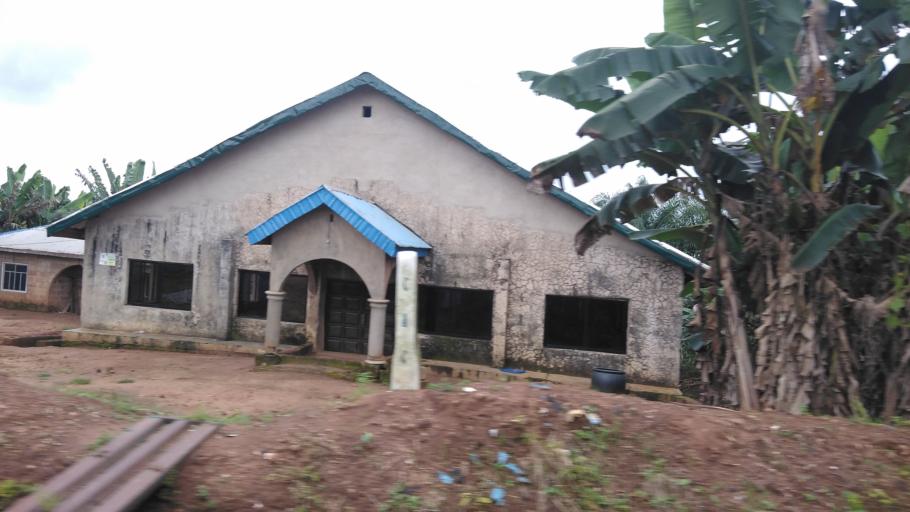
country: NG
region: Ogun
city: Abigi
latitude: 6.5962
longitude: 4.4957
